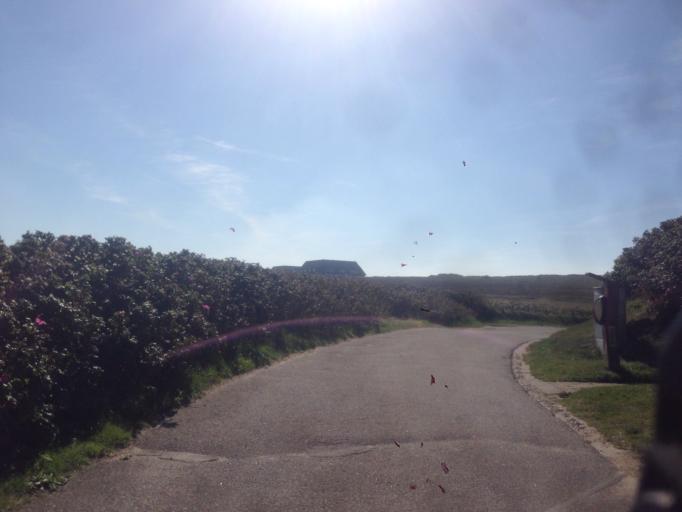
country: DE
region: Schleswig-Holstein
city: Westerland
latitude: 54.9611
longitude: 8.3334
